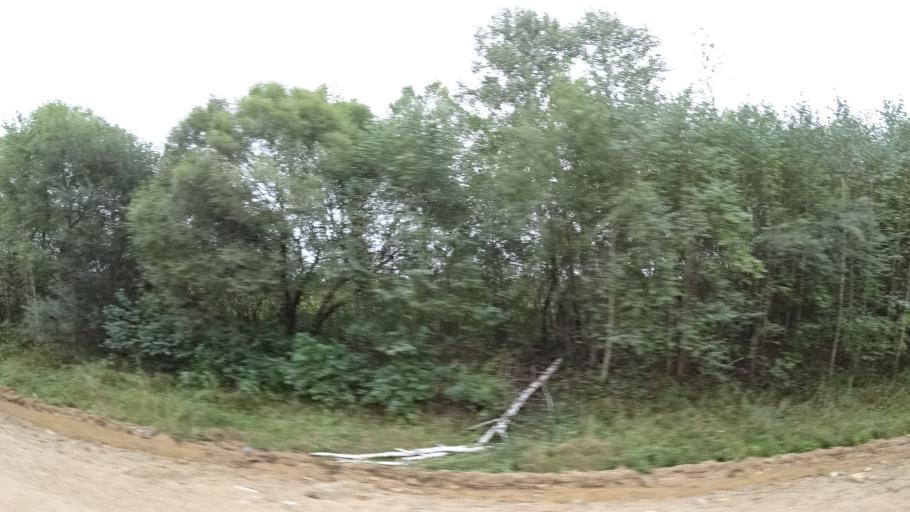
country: RU
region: Primorskiy
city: Rettikhovka
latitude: 44.1481
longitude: 132.6768
